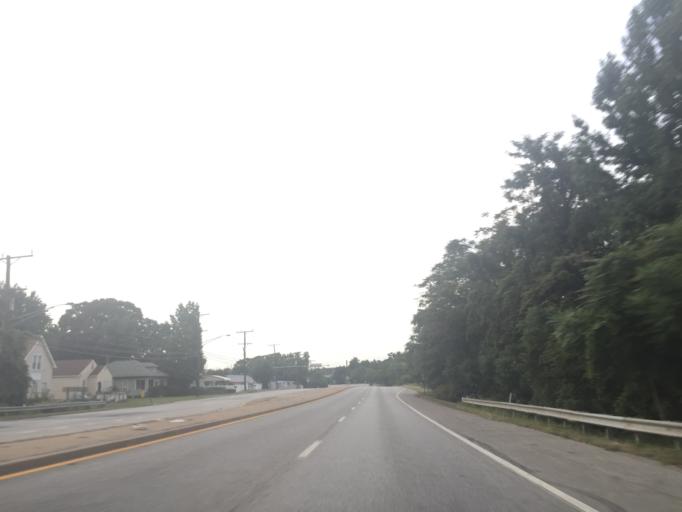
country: US
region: Maryland
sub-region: Anne Arundel County
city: Riviera Beach
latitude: 39.1935
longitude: -76.5546
